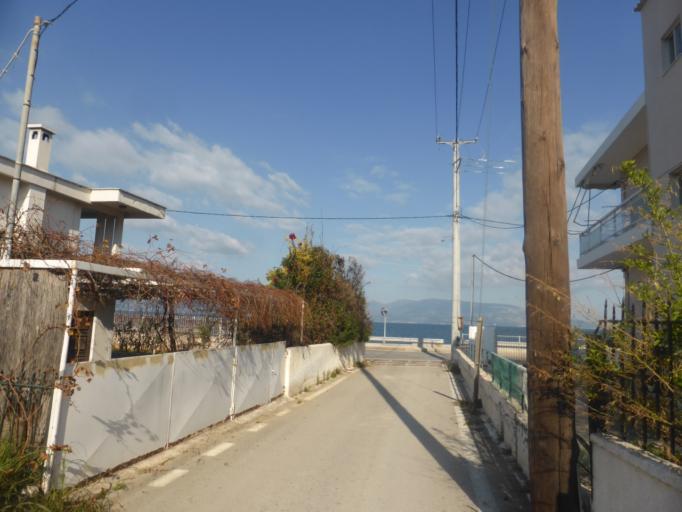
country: GR
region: Attica
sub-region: Nomarchia Anatolikis Attikis
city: Kalamos
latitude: 38.3074
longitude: 23.8678
